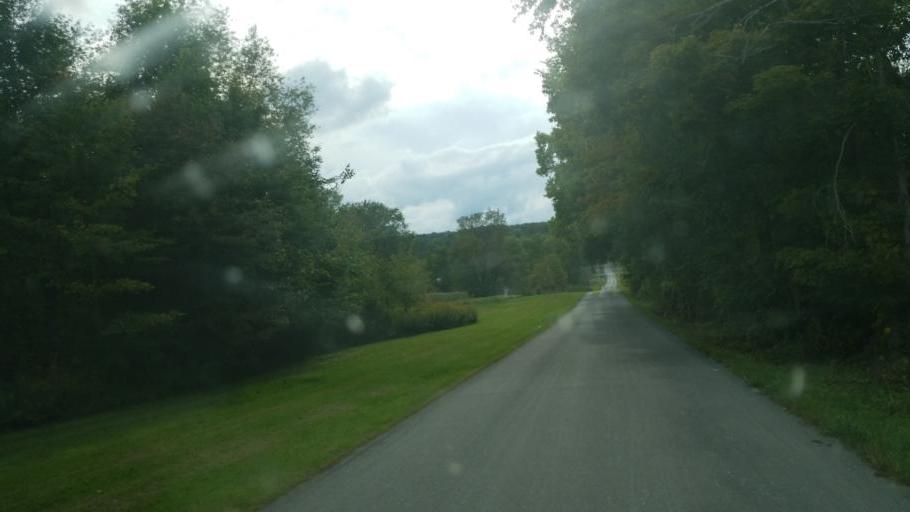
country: US
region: Pennsylvania
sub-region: Mercer County
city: Greenville
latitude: 41.4751
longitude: -80.3603
